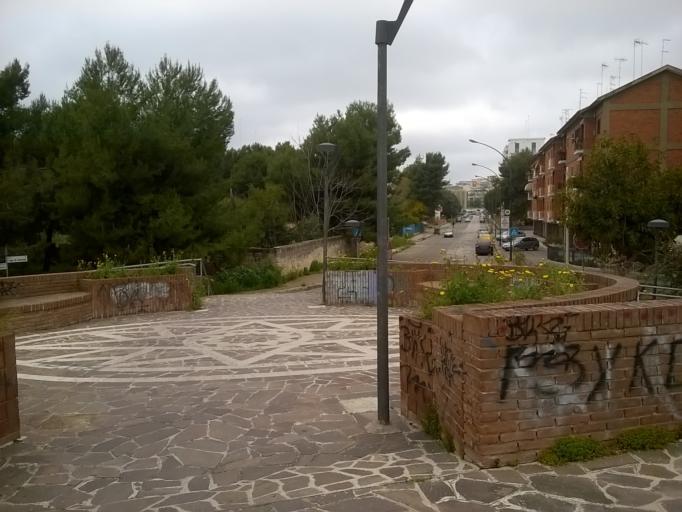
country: IT
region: Apulia
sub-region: Provincia di Taranto
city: Taranto
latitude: 40.4480
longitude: 17.2598
